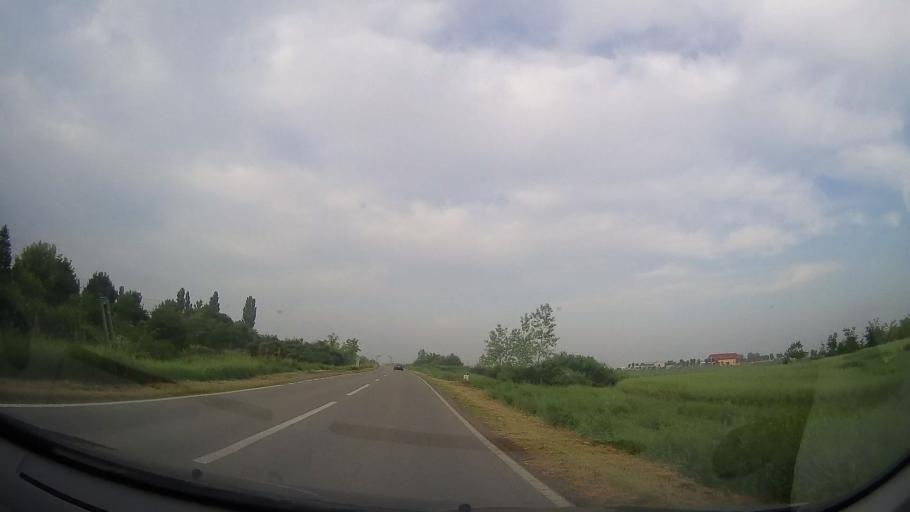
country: RO
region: Timis
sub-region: Comuna Parta
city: Parta
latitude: 45.6327
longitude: 21.1025
